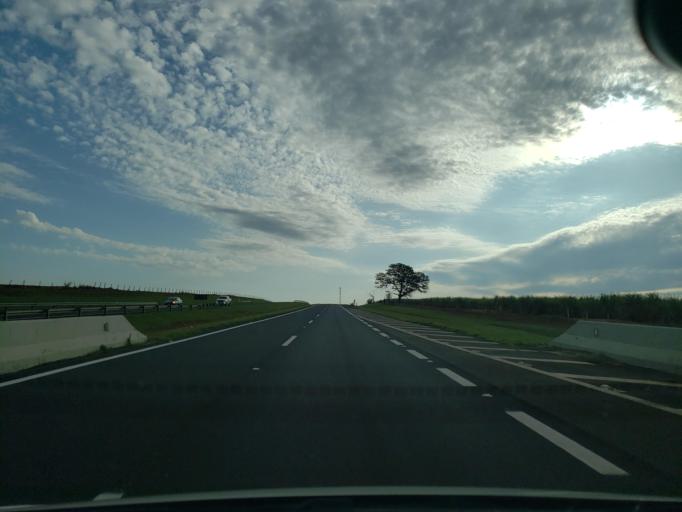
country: BR
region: Sao Paulo
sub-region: Valparaiso
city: Valparaiso
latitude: -21.2074
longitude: -50.7558
